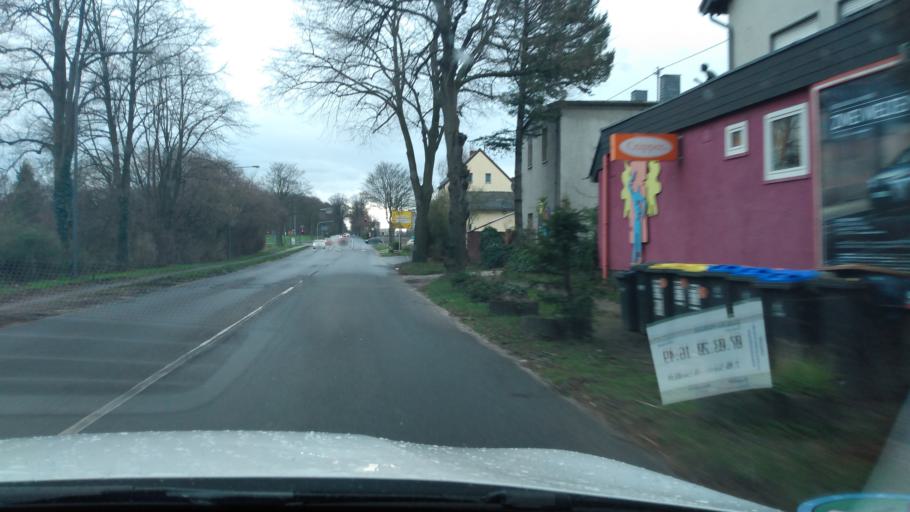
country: DE
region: North Rhine-Westphalia
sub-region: Regierungsbezirk Koln
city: Bayenthal
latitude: 50.8790
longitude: 6.9362
